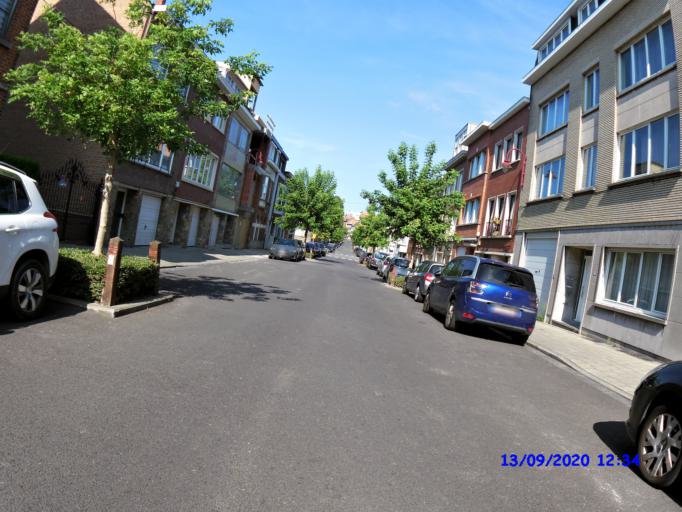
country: BE
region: Flanders
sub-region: Provincie Vlaams-Brabant
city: Wemmel
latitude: 50.8633
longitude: 4.3049
